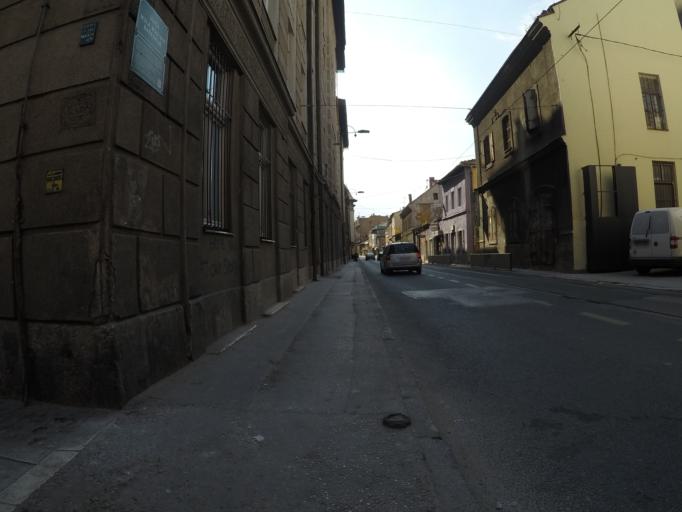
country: BA
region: Federation of Bosnia and Herzegovina
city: Kobilja Glava
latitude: 43.8601
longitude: 18.4296
